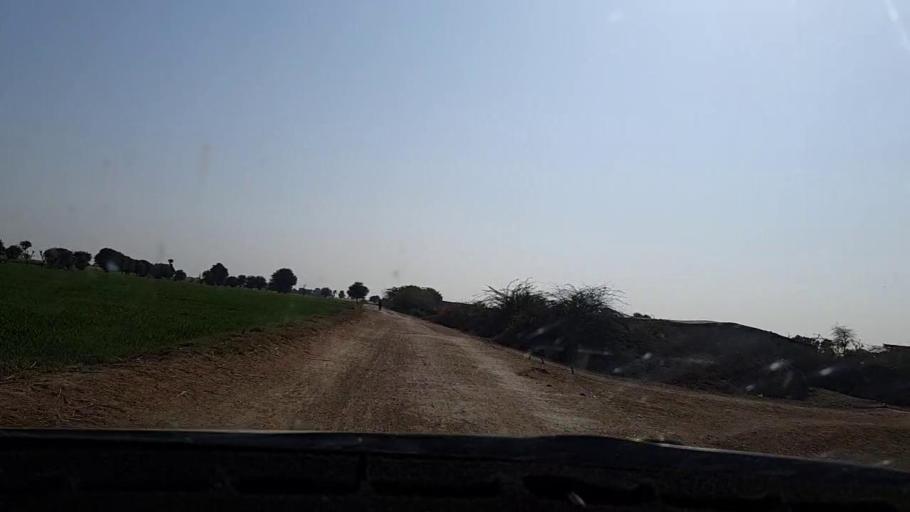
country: PK
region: Sindh
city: Tando Mittha Khan
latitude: 25.8159
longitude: 69.3013
